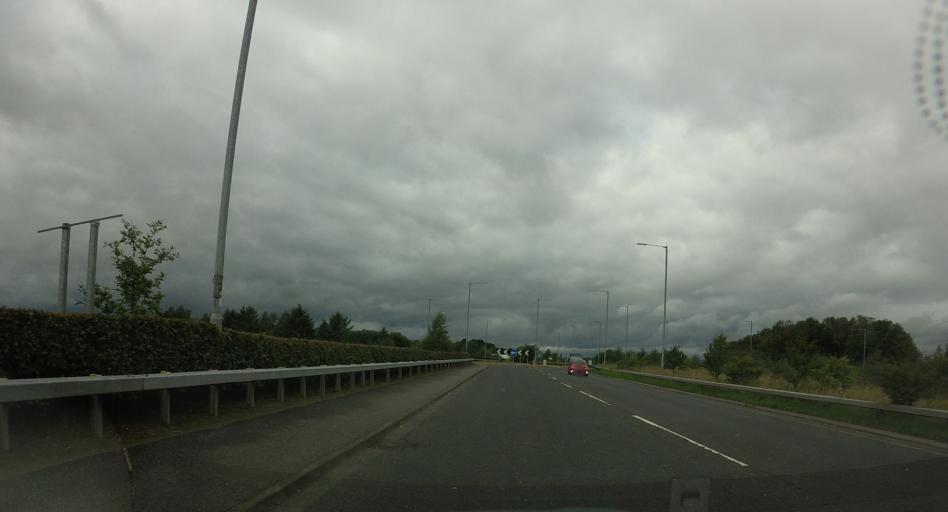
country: GB
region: Scotland
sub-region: Clackmannanshire
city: Clackmannan
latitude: 56.1148
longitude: -3.7676
